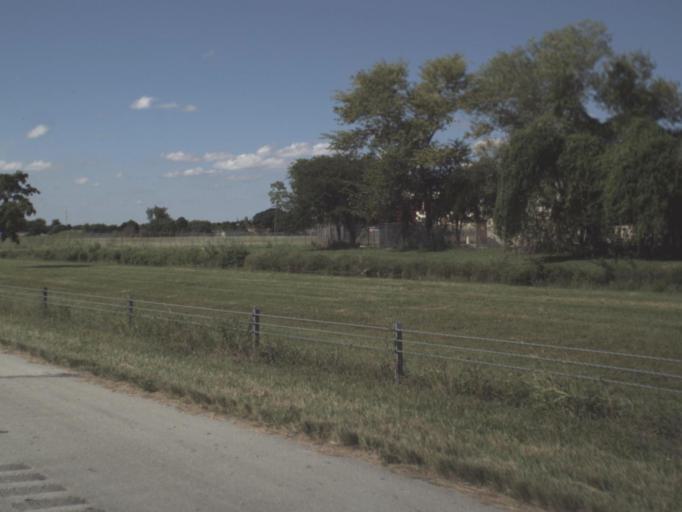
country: US
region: Florida
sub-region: Miami-Dade County
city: Leisure City
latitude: 25.4868
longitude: -80.4260
